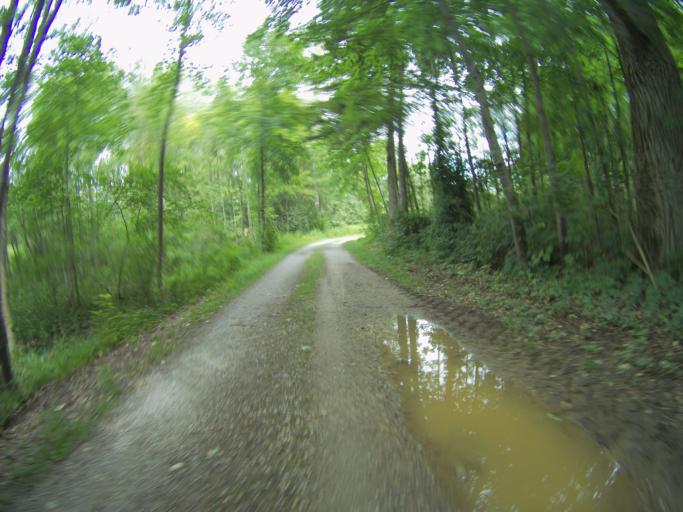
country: DE
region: Bavaria
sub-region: Upper Bavaria
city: Freising
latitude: 48.3781
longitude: 11.7402
